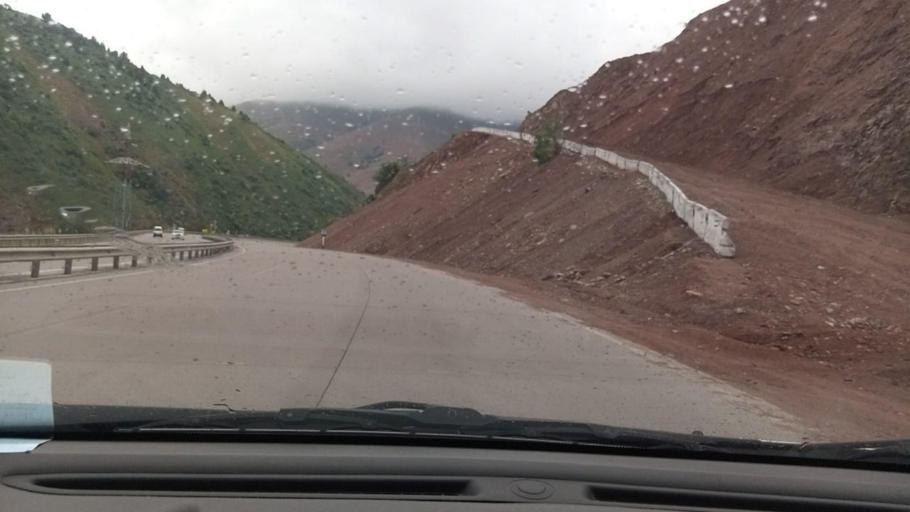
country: UZ
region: Toshkent
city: Angren
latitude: 41.1444
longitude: 70.4484
